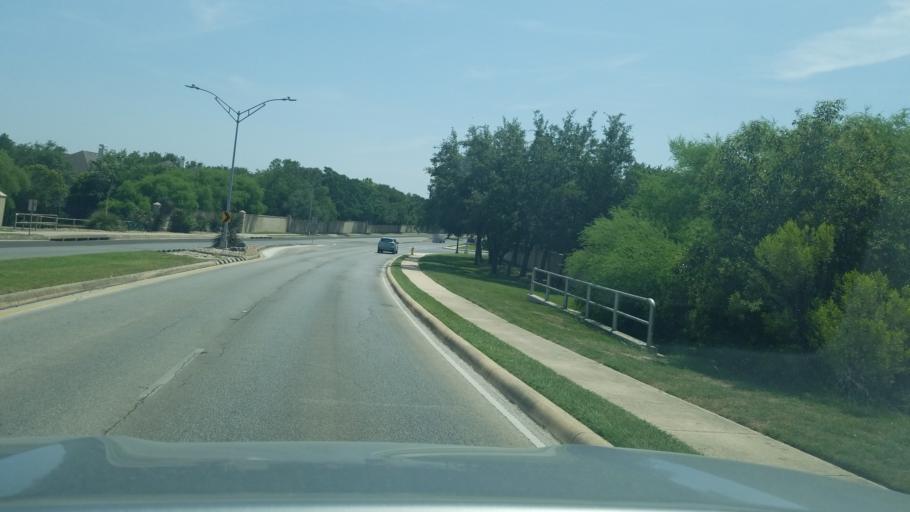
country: US
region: Texas
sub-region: Bexar County
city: Hollywood Park
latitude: 29.6164
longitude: -98.5173
